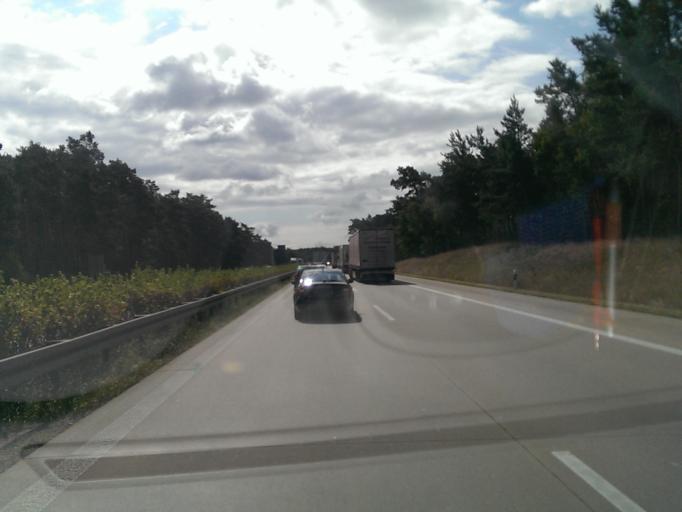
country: DE
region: Brandenburg
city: Kasel-Golzig
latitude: 52.0090
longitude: 13.7100
